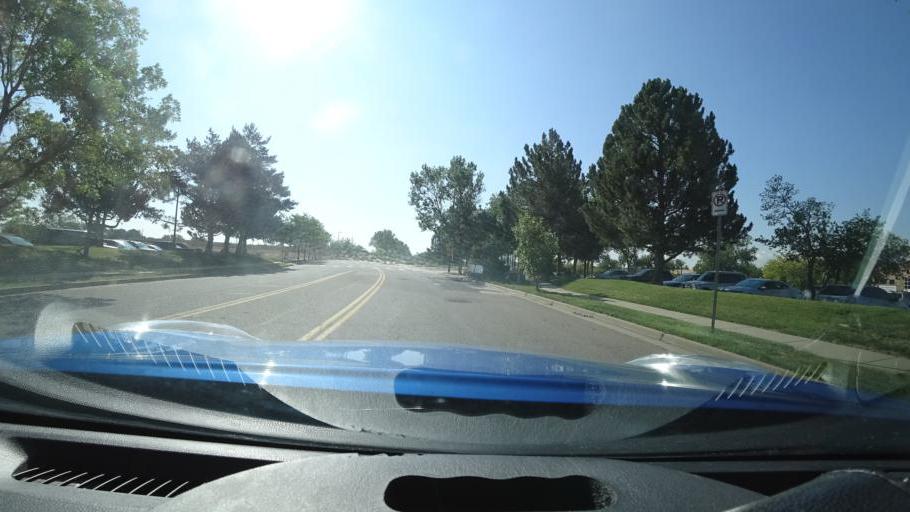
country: US
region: Colorado
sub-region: Adams County
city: Aurora
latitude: 39.7192
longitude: -104.8025
